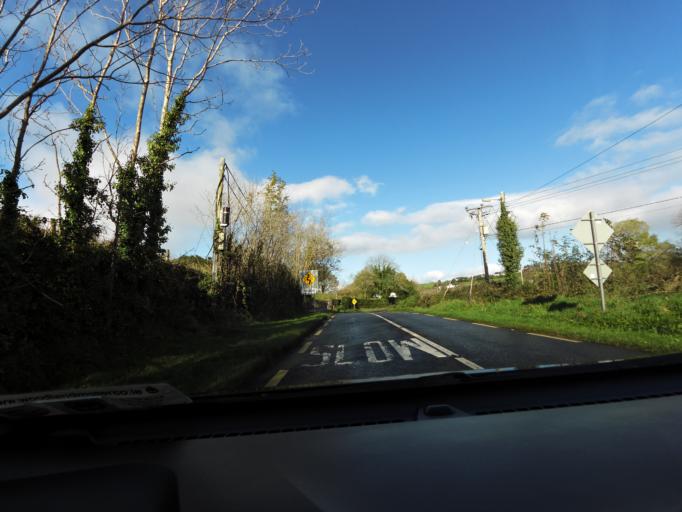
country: IE
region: Connaught
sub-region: Maigh Eo
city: Westport
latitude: 53.8080
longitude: -9.5280
